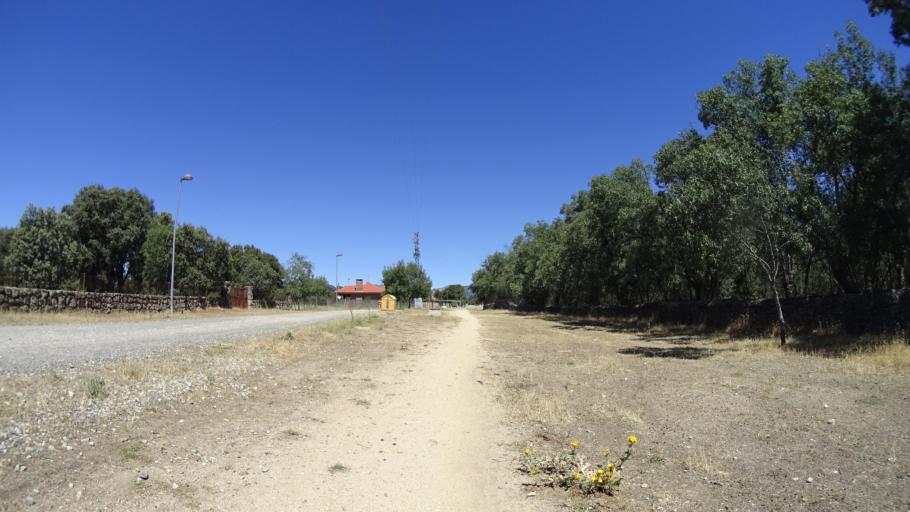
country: ES
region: Madrid
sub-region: Provincia de Madrid
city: Alpedrete
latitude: 40.6501
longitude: -4.0403
